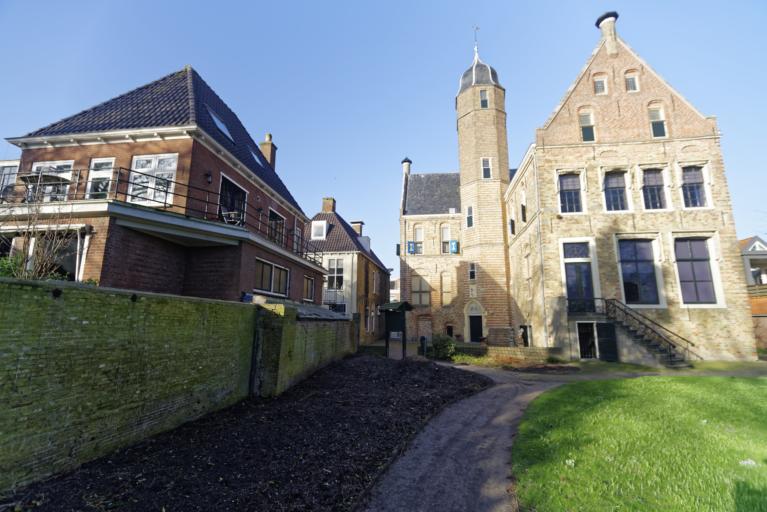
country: NL
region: Friesland
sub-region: Gemeente Franekeradeel
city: Franeker
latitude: 53.1861
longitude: 5.5421
